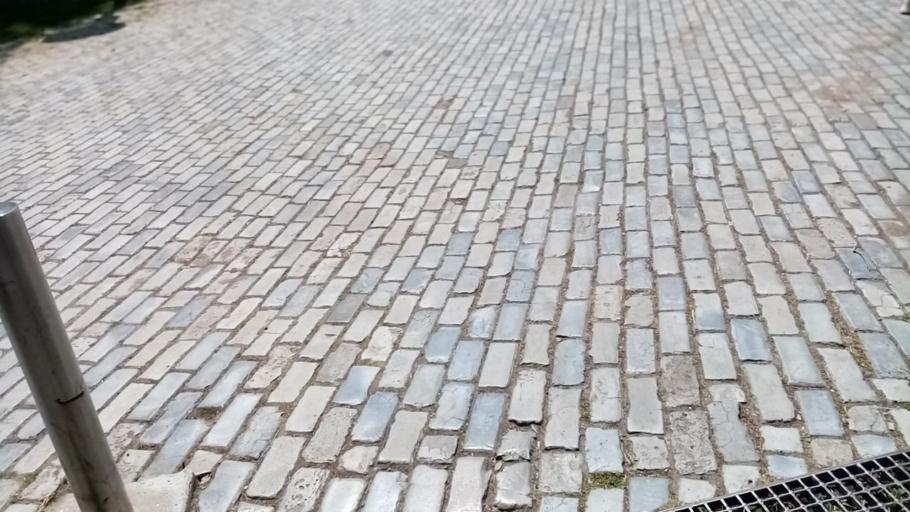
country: NL
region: South Holland
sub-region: Gemeente Rotterdam
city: Rotterdam
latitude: 51.9113
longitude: 4.4730
